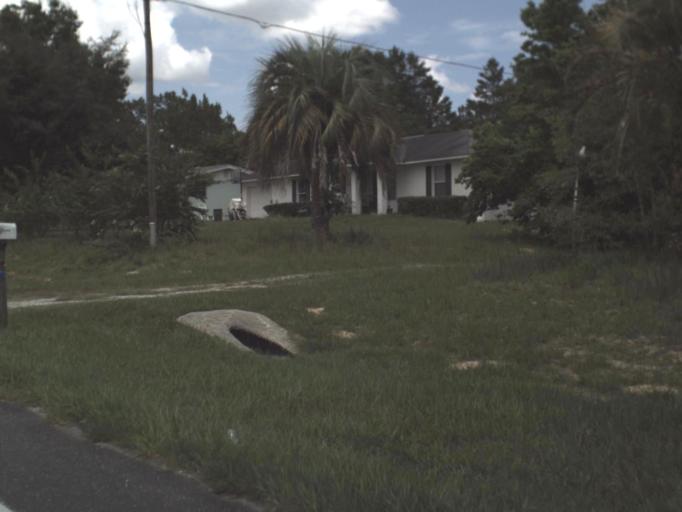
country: US
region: Florida
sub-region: Levy County
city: Williston Highlands
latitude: 29.3517
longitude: -82.5076
